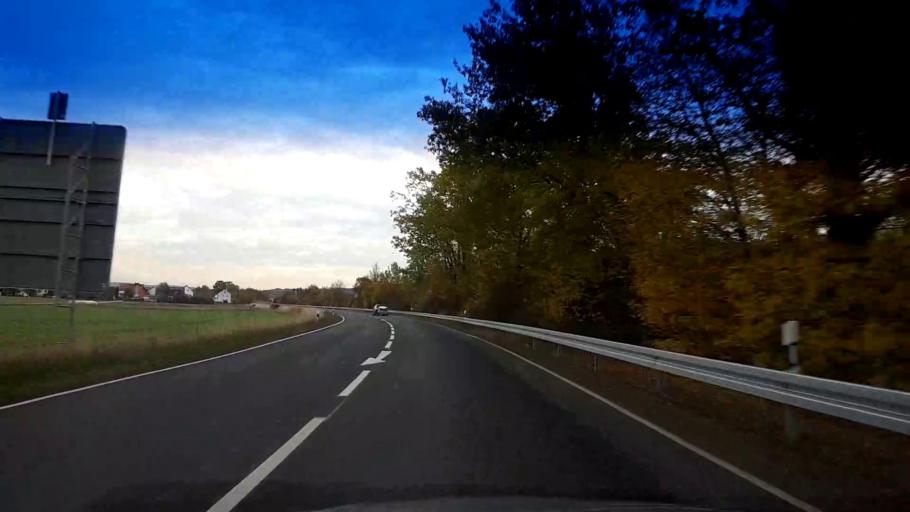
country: DE
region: Bavaria
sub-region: Upper Franconia
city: Priesendorf
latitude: 49.9328
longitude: 10.7389
